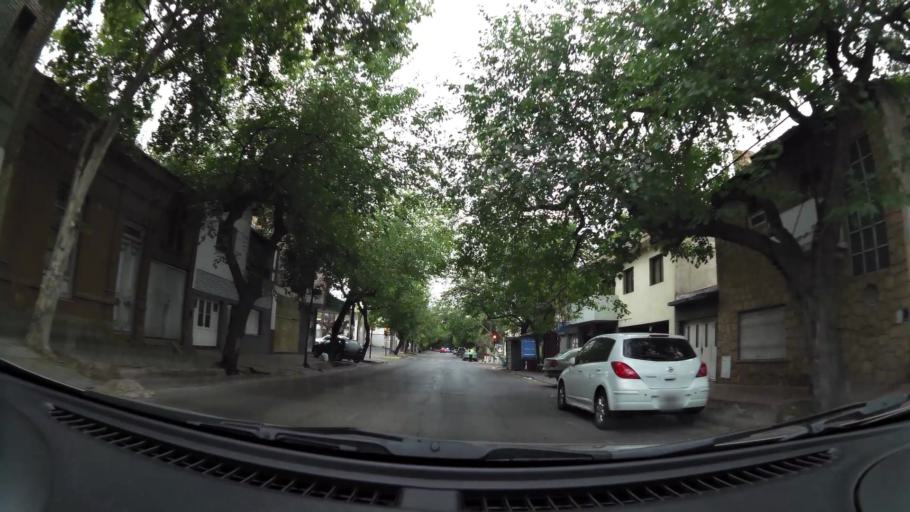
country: AR
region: Mendoza
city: Mendoza
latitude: -32.8796
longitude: -68.8574
